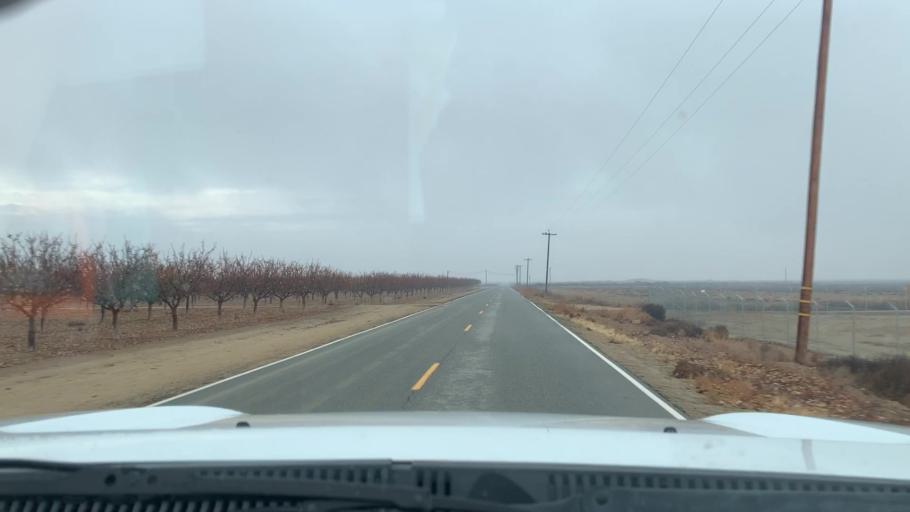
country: US
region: California
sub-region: Kern County
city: Lost Hills
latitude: 35.6333
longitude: -119.5800
